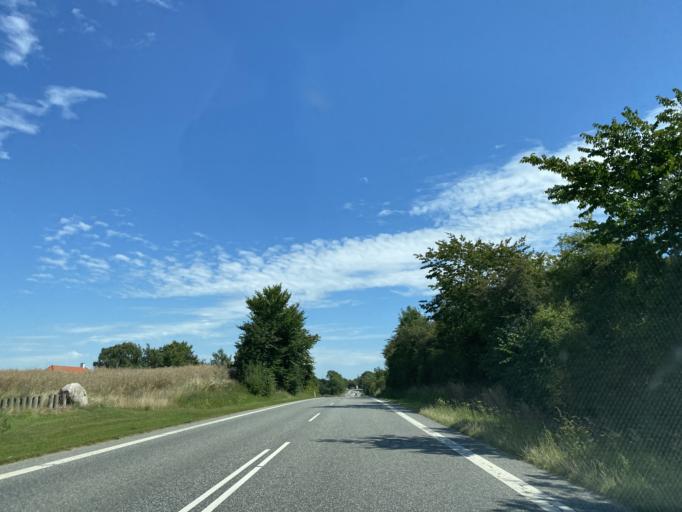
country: DK
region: South Denmark
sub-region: Faaborg-Midtfyn Kommune
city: Faaborg
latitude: 55.1086
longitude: 10.1482
